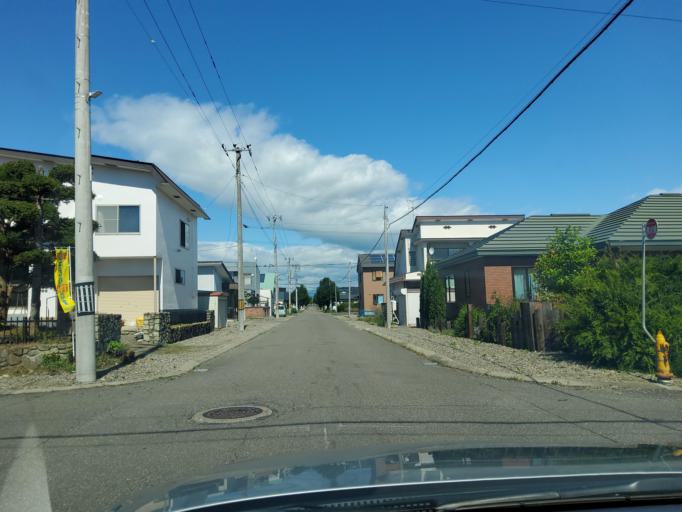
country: JP
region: Hokkaido
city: Otofuke
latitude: 42.9579
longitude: 143.1921
